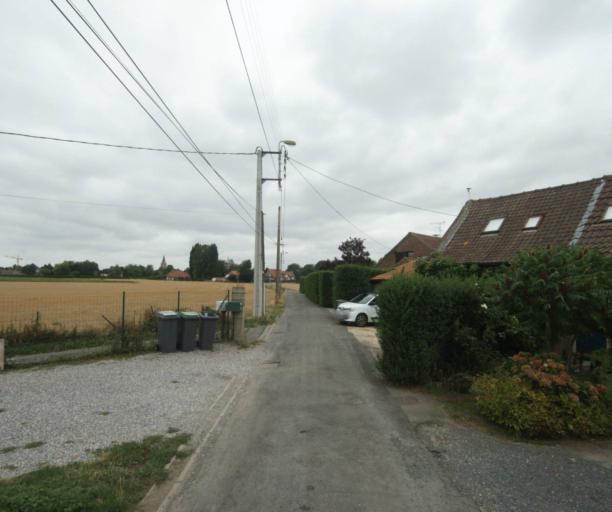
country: FR
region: Nord-Pas-de-Calais
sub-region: Departement du Nord
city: Leers
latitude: 50.6800
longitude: 3.2590
